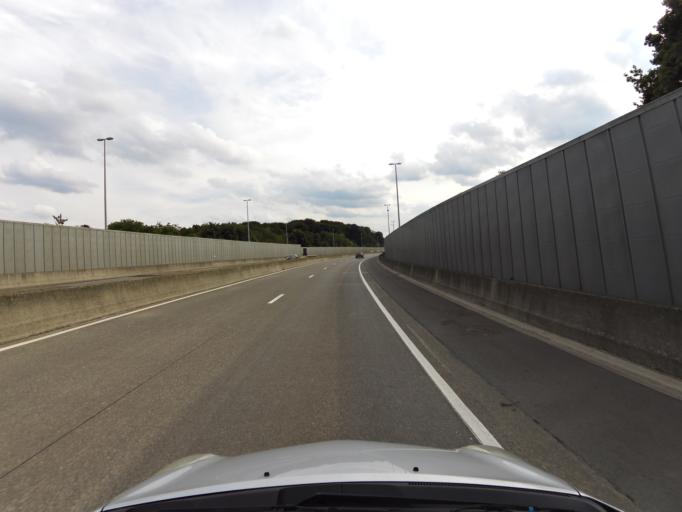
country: BE
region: Flanders
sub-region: Provincie West-Vlaanderen
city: Brugge
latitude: 51.1846
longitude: 3.2023
